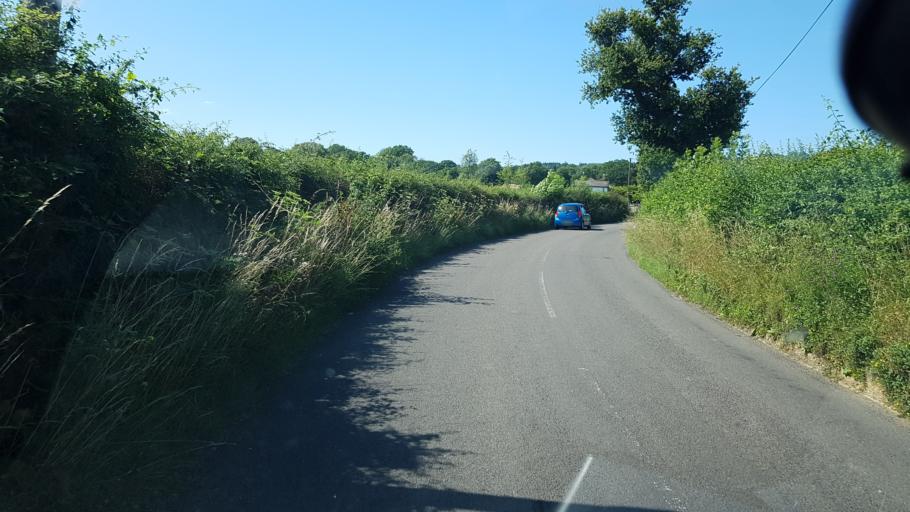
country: GB
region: England
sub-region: Kent
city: Edenbridge
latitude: 51.2261
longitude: 0.0741
